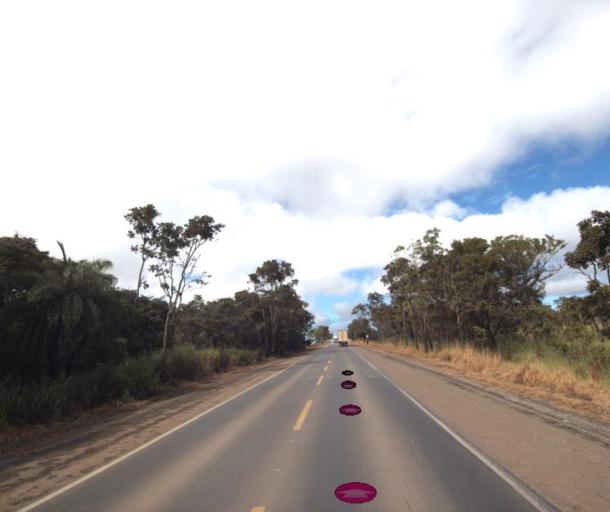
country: BR
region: Goias
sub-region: Uruacu
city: Uruacu
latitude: -14.7577
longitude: -49.2578
